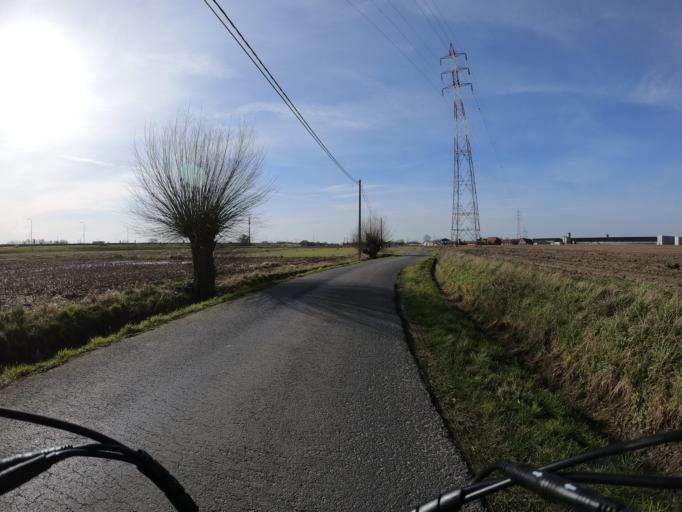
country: BE
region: Flanders
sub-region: Provincie West-Vlaanderen
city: Menen
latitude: 50.8188
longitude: 3.1319
